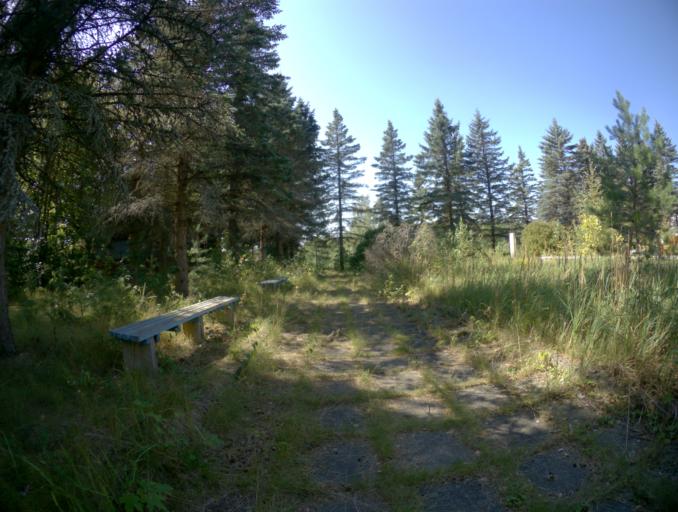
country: RU
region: Vladimir
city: Sobinka
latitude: 55.9427
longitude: 39.9853
